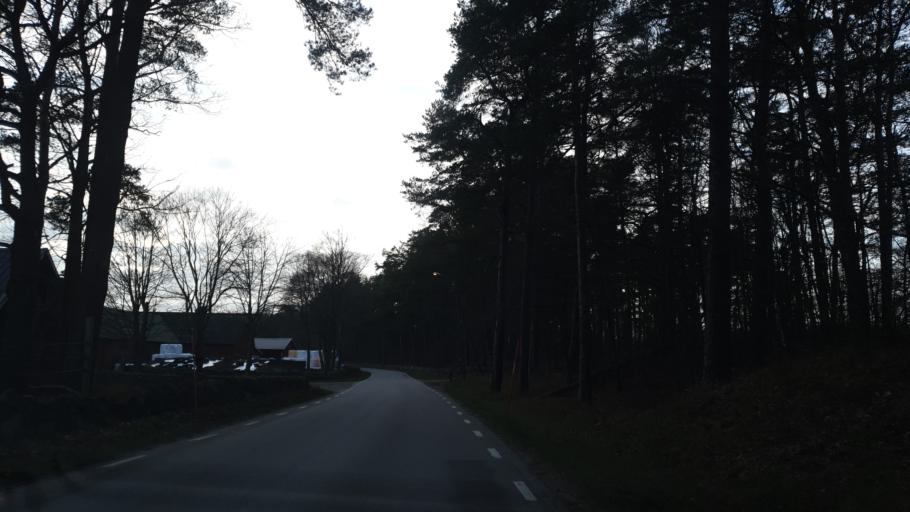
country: SE
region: Blekinge
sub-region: Karlskrona Kommun
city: Jaemjoe
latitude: 56.2047
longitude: 15.9607
